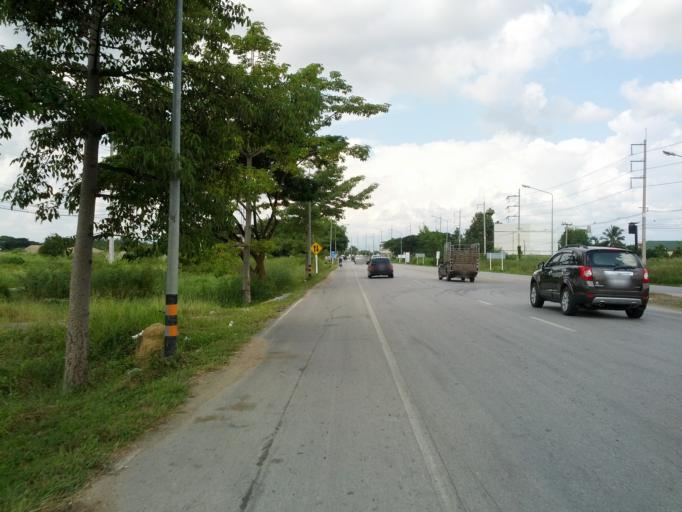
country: TH
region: Chiang Mai
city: San Kamphaeng
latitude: 18.7738
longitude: 99.0684
